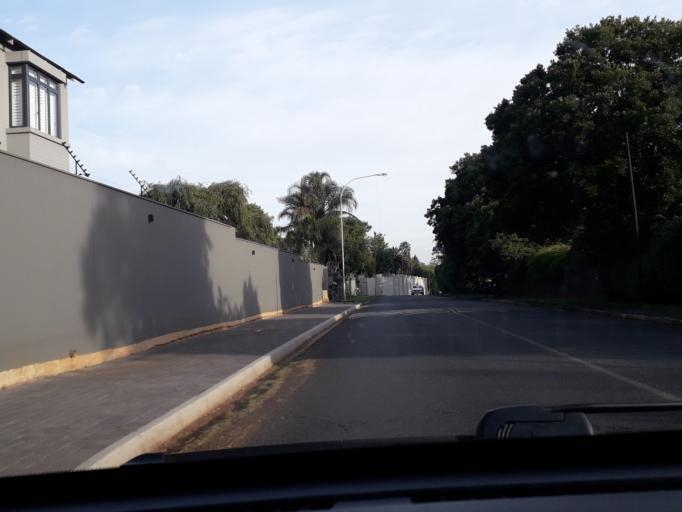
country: ZA
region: Gauteng
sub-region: City of Johannesburg Metropolitan Municipality
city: Johannesburg
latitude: -26.1531
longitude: 28.0645
